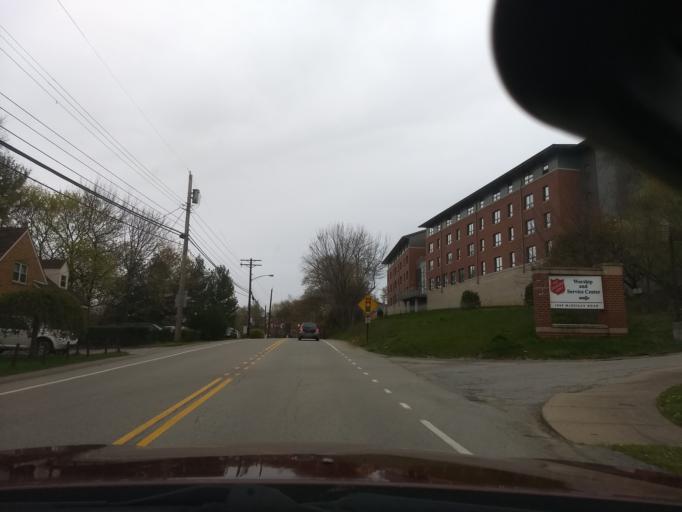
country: US
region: Pennsylvania
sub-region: Allegheny County
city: Dormont
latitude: 40.3898
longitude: -80.0286
